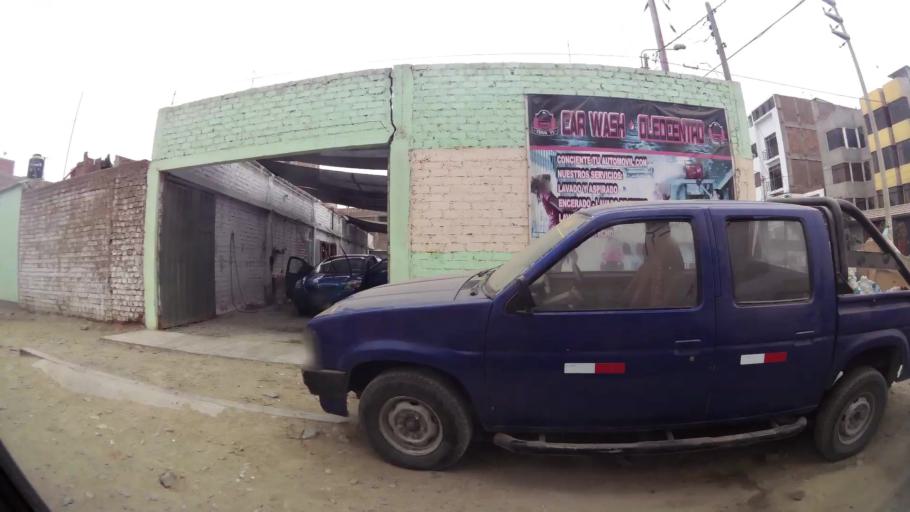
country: PE
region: La Libertad
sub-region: Provincia de Trujillo
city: Buenos Aires
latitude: -8.1234
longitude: -79.0452
